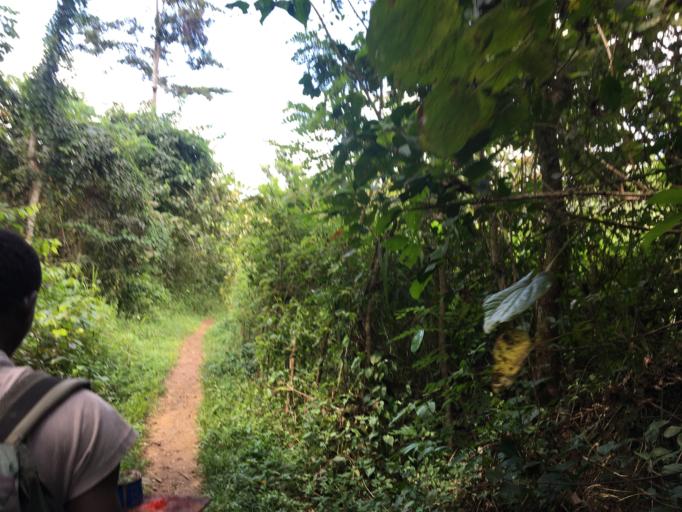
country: TG
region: Plateaux
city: Kpalime
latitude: 6.9721
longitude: 0.5736
